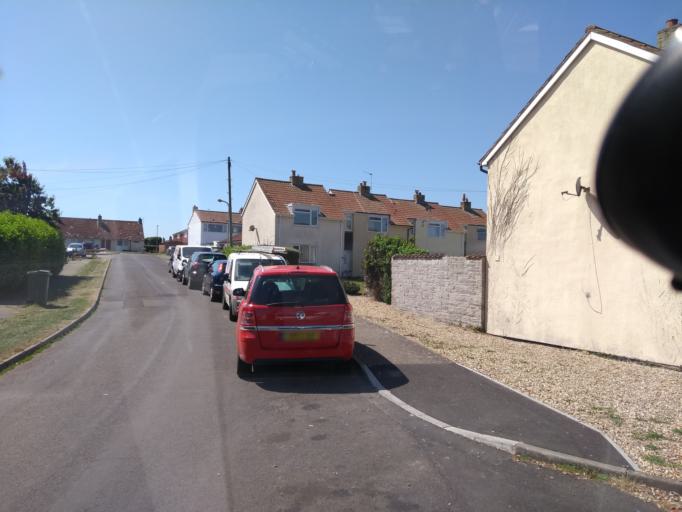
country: GB
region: England
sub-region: Somerset
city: Woolavington
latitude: 51.1639
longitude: -2.9389
